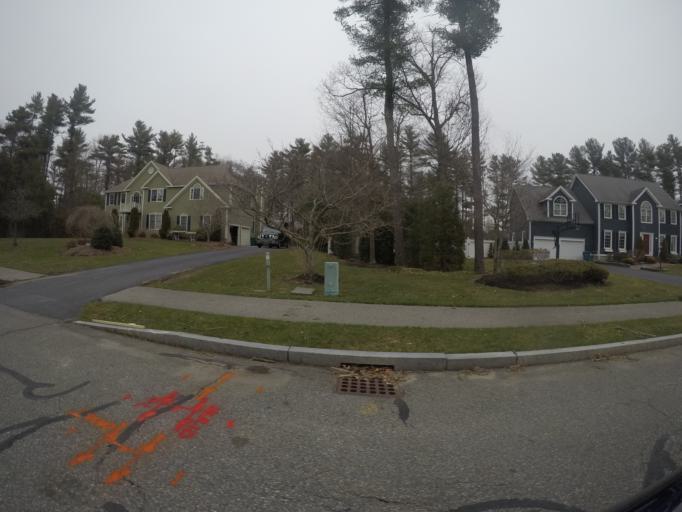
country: US
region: Massachusetts
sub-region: Bristol County
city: Easton
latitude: 42.0193
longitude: -71.1134
